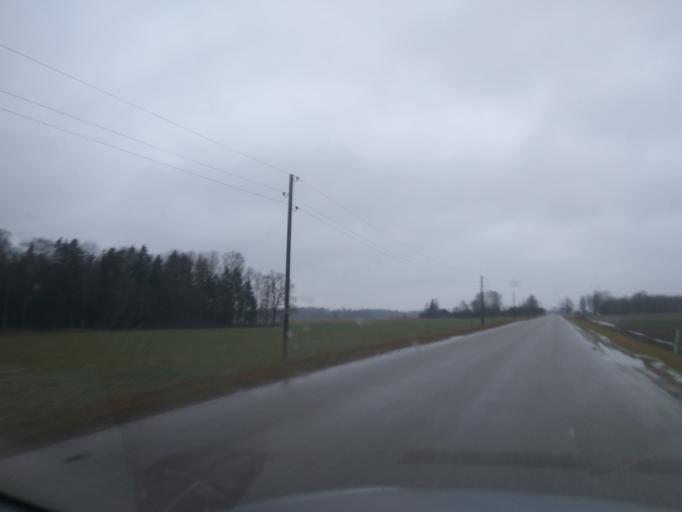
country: LV
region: Saldus Rajons
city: Saldus
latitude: 56.8317
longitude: 22.3759
